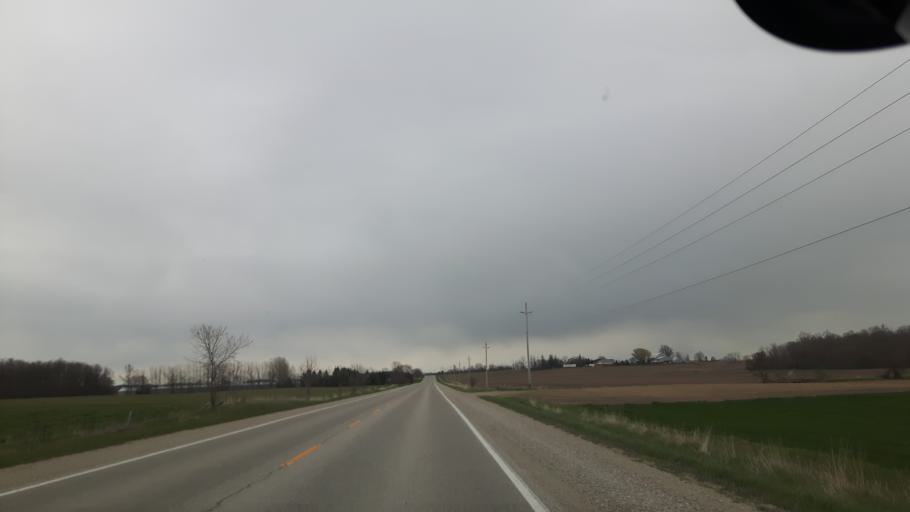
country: CA
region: Ontario
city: Bluewater
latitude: 43.5868
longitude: -81.6145
